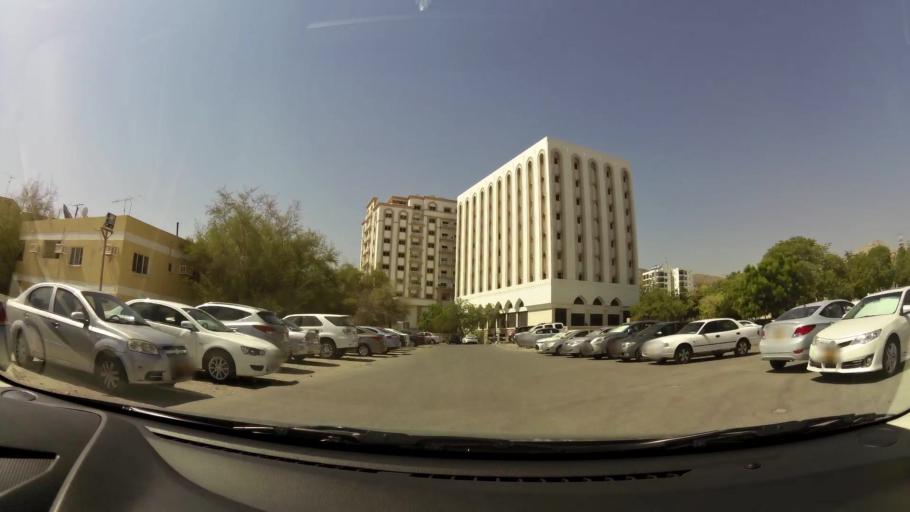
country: OM
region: Muhafazat Masqat
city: Muscat
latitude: 23.6011
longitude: 58.5382
